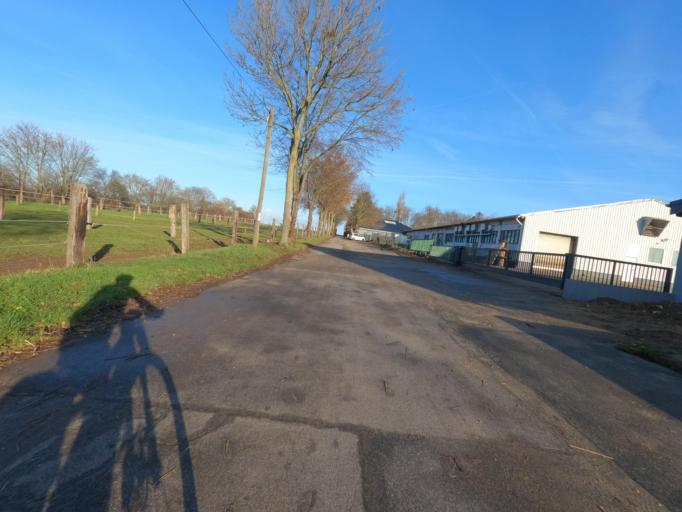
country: DE
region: North Rhine-Westphalia
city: Julich
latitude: 50.9268
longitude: 6.3978
